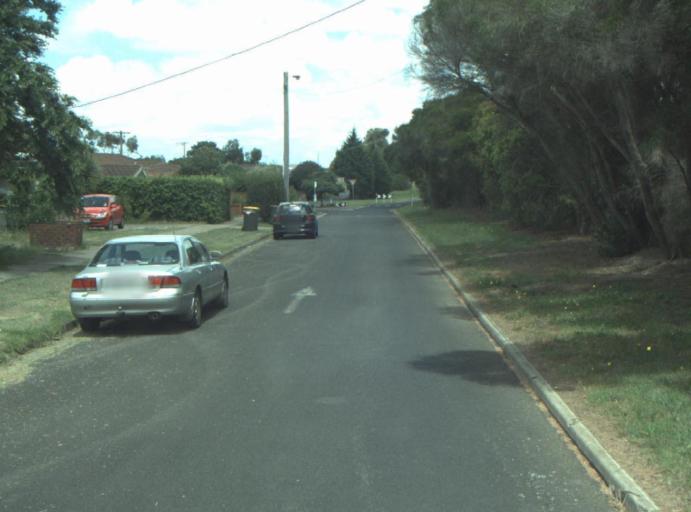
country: AU
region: Victoria
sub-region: Greater Geelong
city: Wandana Heights
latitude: -38.1883
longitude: 144.3291
